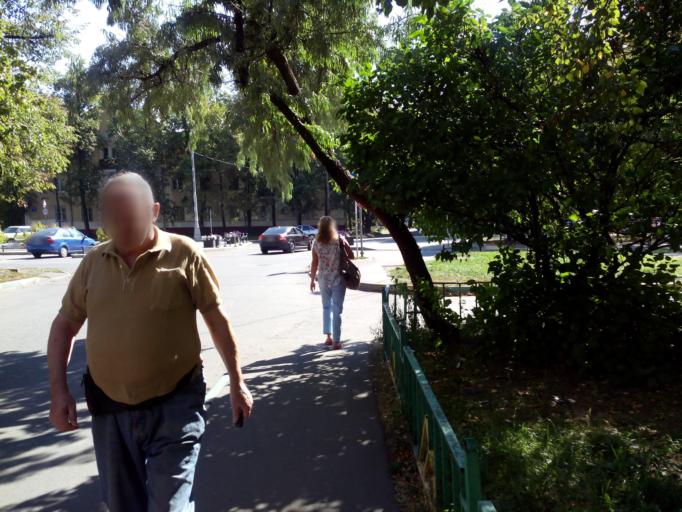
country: RU
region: Moskovskaya
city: Bol'shaya Setun'
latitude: 55.7313
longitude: 37.4167
